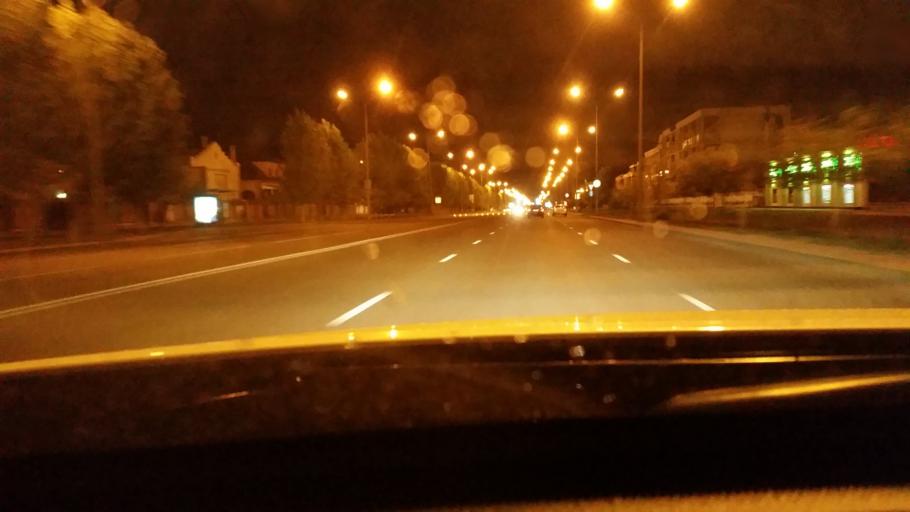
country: KZ
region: Astana Qalasy
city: Astana
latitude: 51.1440
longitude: 71.4866
